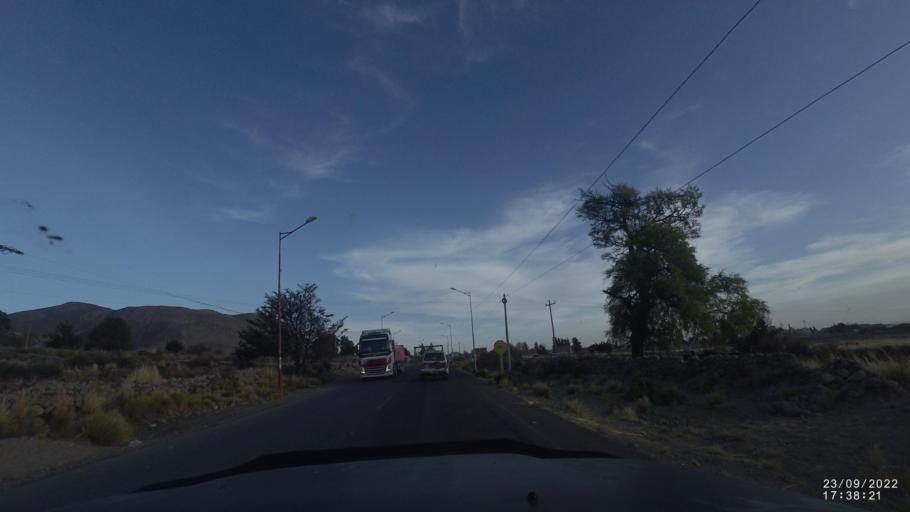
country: BO
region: Oruro
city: Challapata
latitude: -19.0038
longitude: -66.7765
